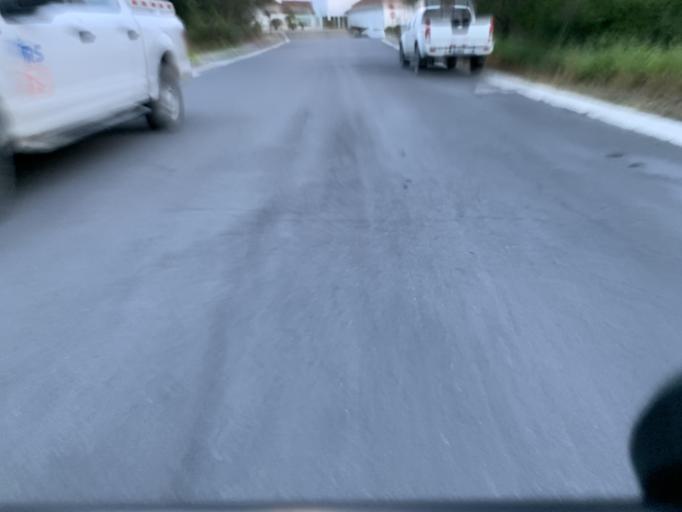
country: MX
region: Nuevo Leon
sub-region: Juarez
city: Bosques de San Pedro
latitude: 25.5211
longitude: -100.1919
